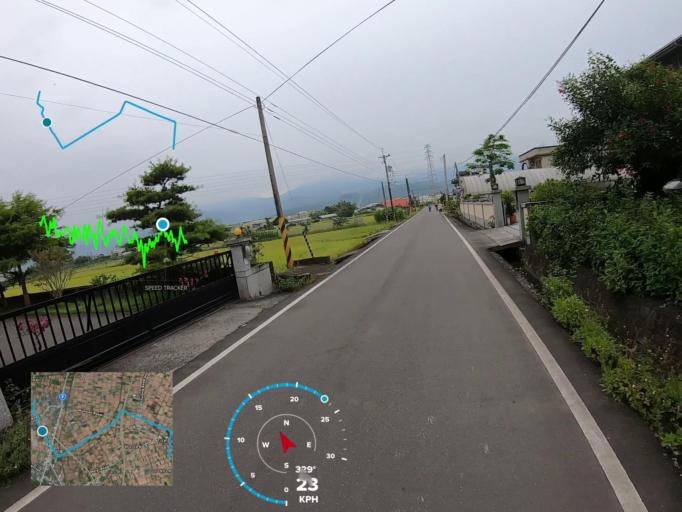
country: TW
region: Taiwan
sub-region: Yilan
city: Yilan
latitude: 24.7801
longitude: 121.7635
